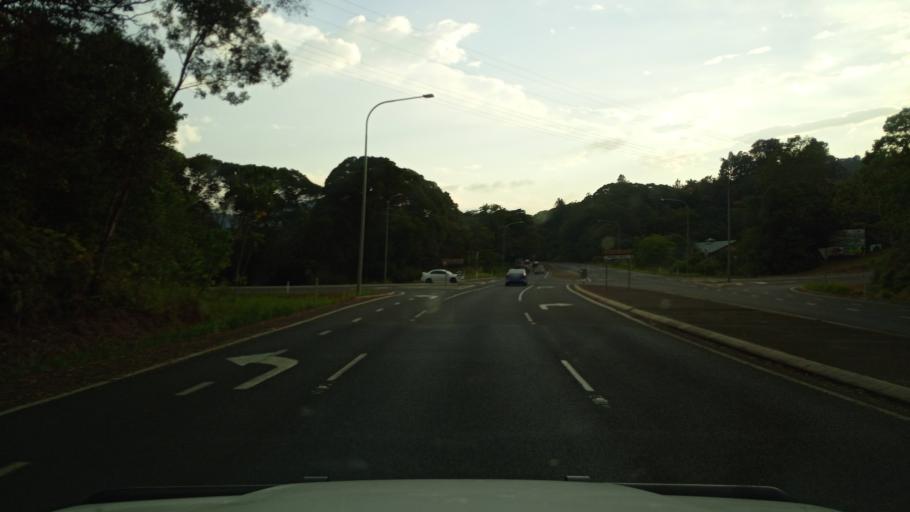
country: AU
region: Queensland
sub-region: Tablelands
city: Kuranda
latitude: -16.8314
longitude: 145.6211
